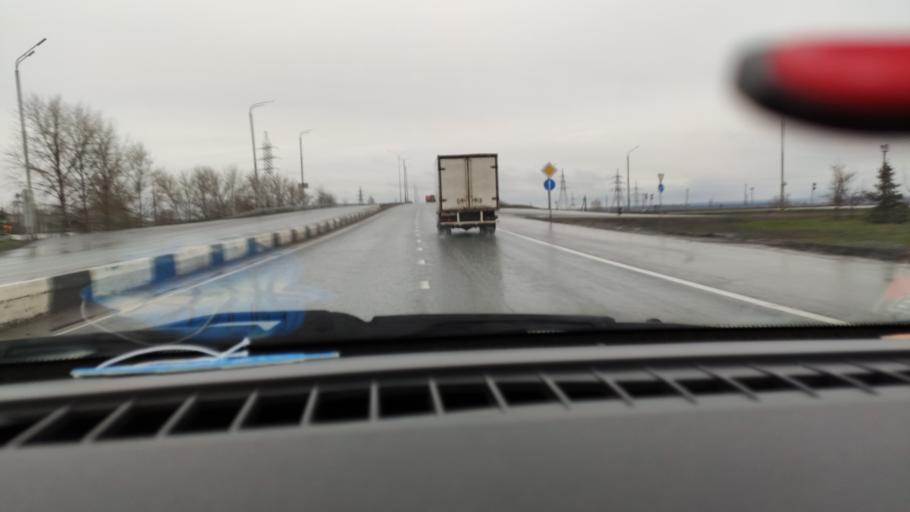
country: RU
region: Tatarstan
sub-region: Tukayevskiy Rayon
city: Naberezhnyye Chelny
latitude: 55.6660
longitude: 52.2696
